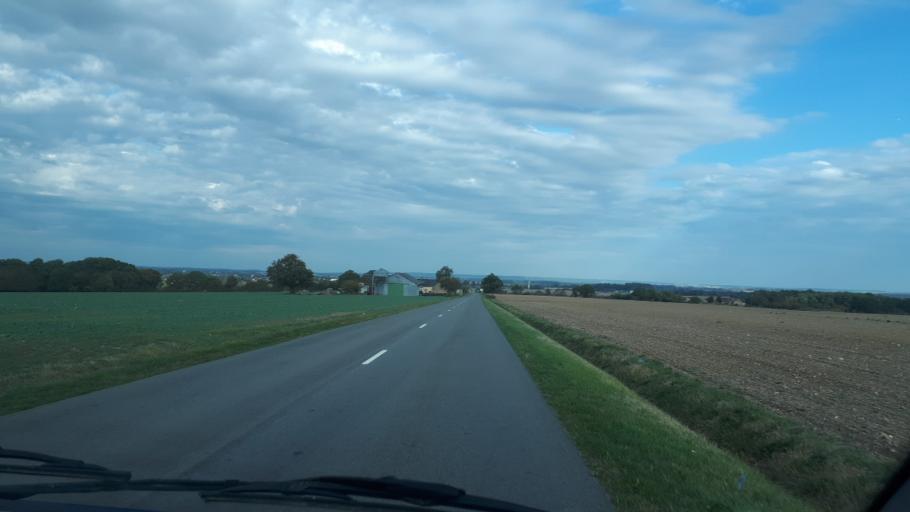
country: FR
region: Centre
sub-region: Departement du Loir-et-Cher
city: Mondoubleau
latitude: 47.9606
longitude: 0.9296
